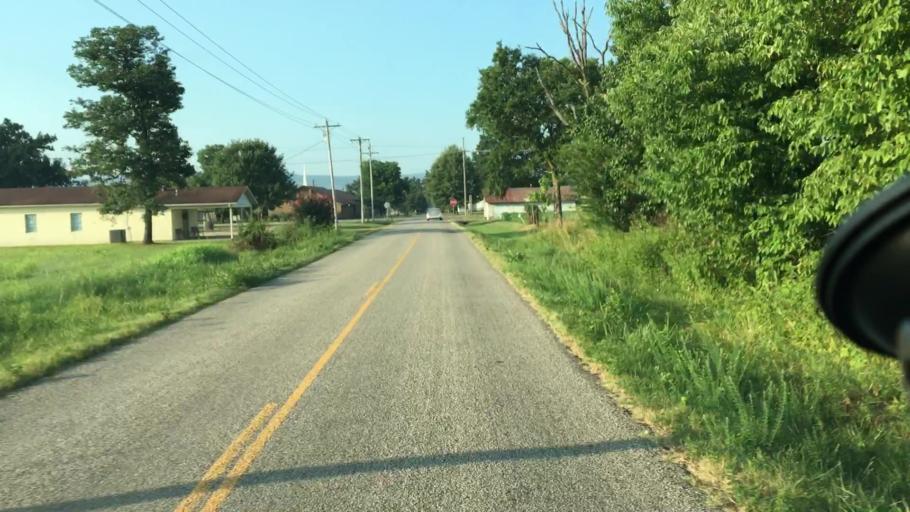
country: US
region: Arkansas
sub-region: Johnson County
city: Coal Hill
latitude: 35.3383
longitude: -93.6138
